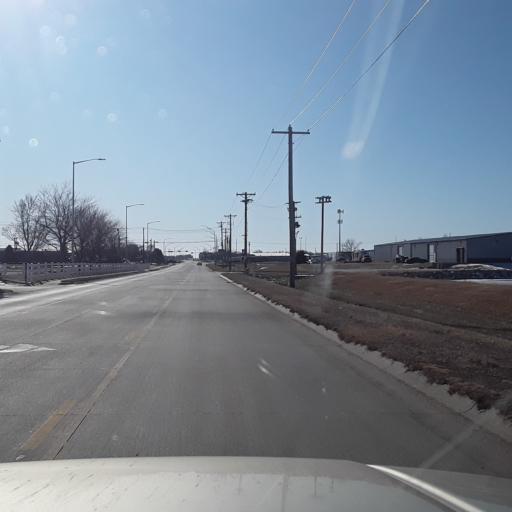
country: US
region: Nebraska
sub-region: Adams County
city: Hastings
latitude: 40.5716
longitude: -98.4021
